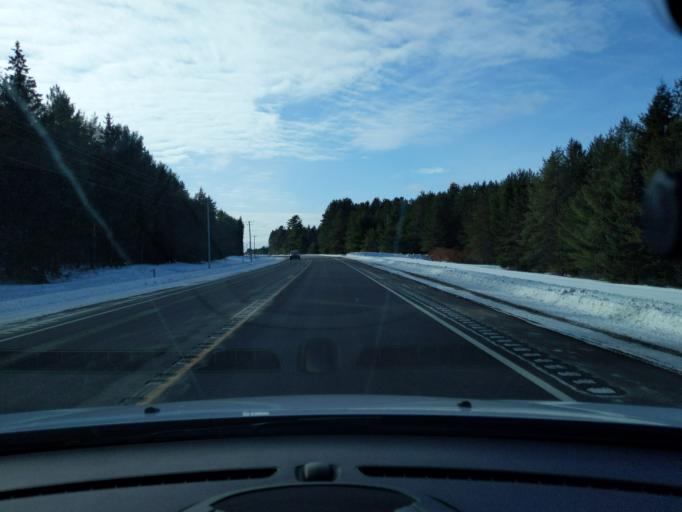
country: US
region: Wisconsin
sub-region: Sawyer County
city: Little Round Lake
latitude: 46.1153
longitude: -91.3682
